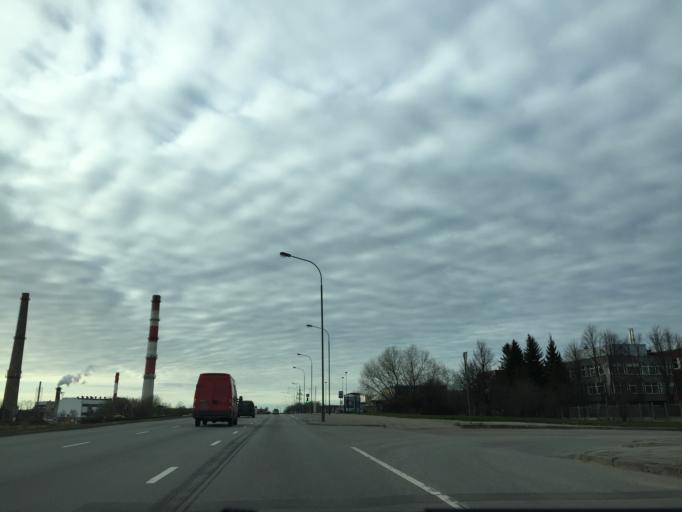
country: LT
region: Klaipedos apskritis
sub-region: Klaipeda
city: Klaipeda
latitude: 55.6942
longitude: 21.1757
